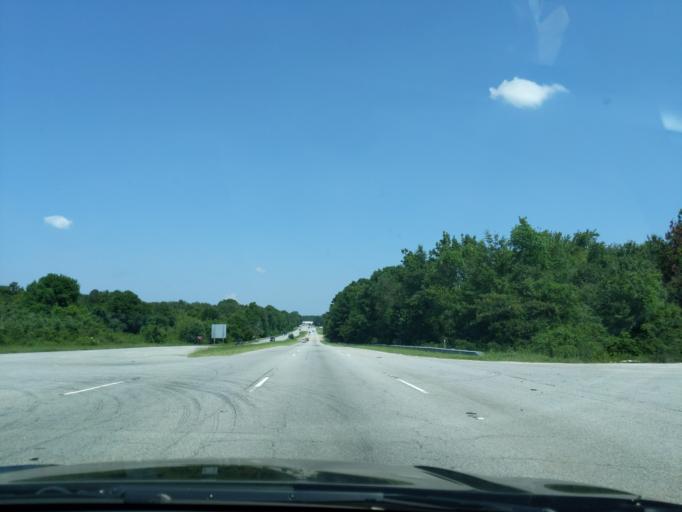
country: US
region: South Carolina
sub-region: Richland County
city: Forest Acres
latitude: 33.9532
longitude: -80.9785
